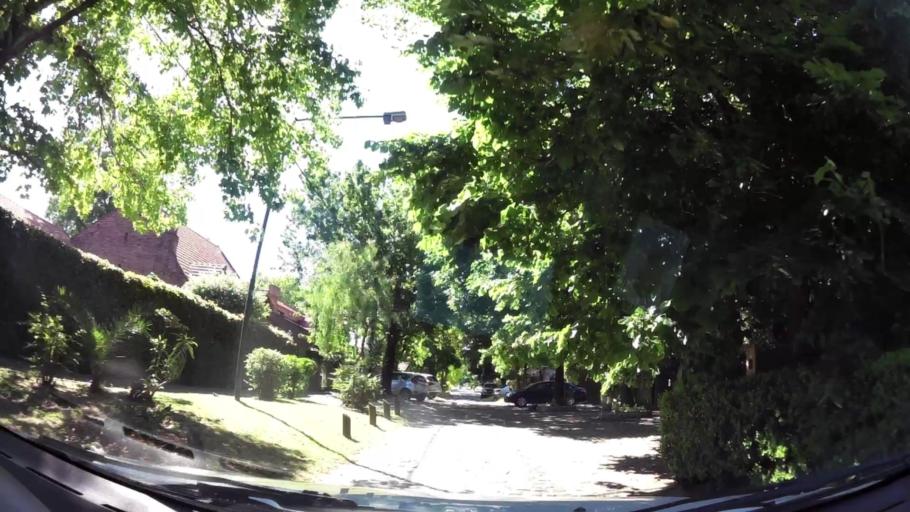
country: AR
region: Buenos Aires
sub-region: Partido de San Isidro
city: San Isidro
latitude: -34.4558
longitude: -58.5269
